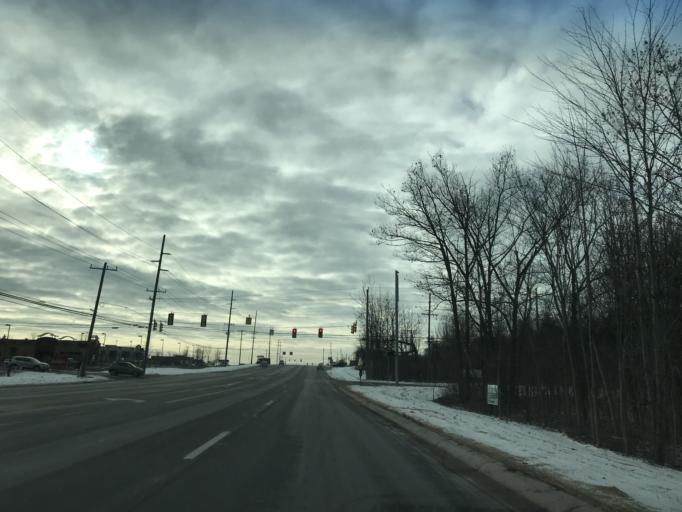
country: US
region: Michigan
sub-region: Oakland County
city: Clarkston
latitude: 42.7417
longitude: -83.3799
